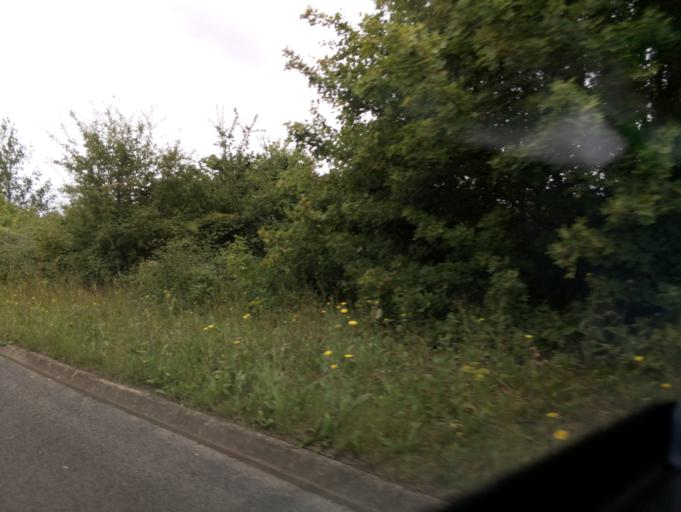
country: GB
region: England
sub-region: Gloucestershire
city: Tewkesbury
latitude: 51.9845
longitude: -2.1461
